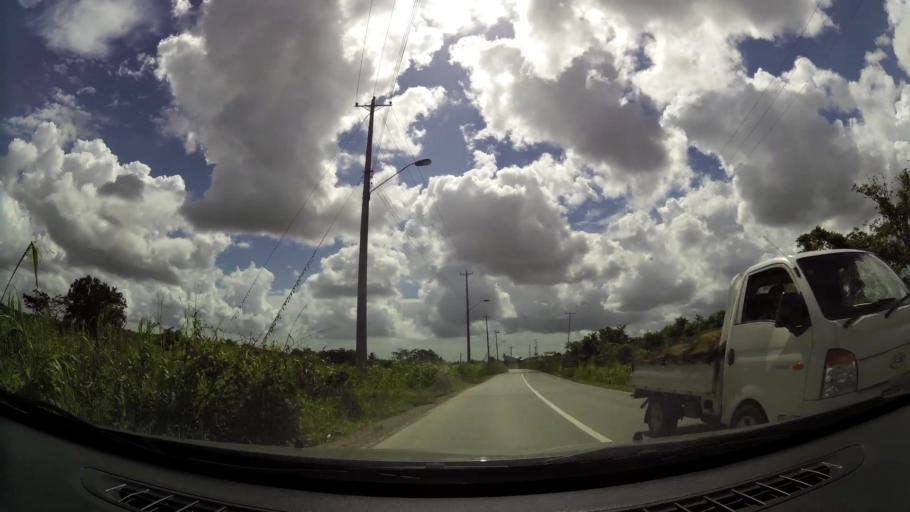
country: TT
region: Penal/Debe
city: Debe
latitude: 10.2286
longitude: -61.4809
